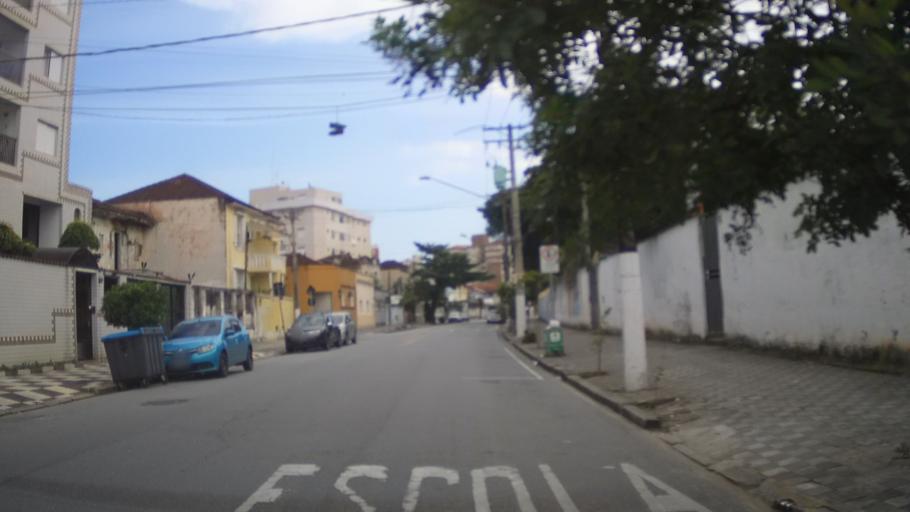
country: BR
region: Sao Paulo
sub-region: Santos
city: Santos
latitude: -23.9524
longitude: -46.3393
